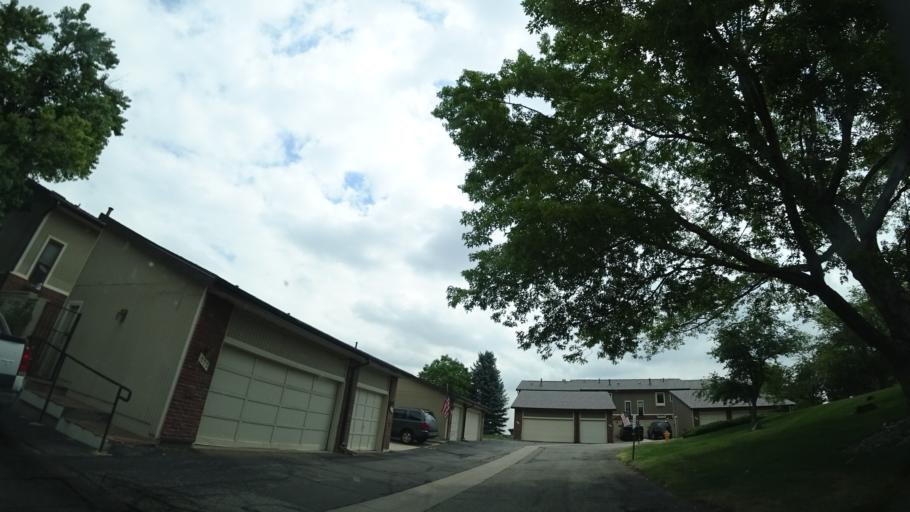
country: US
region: Colorado
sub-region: Jefferson County
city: West Pleasant View
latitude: 39.7141
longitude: -105.1621
